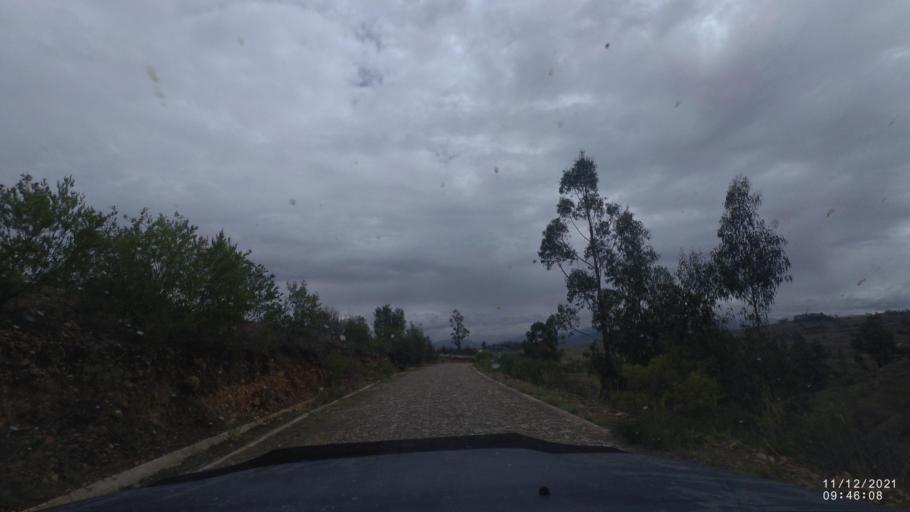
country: BO
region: Cochabamba
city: Tarata
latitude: -17.7884
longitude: -65.9741
